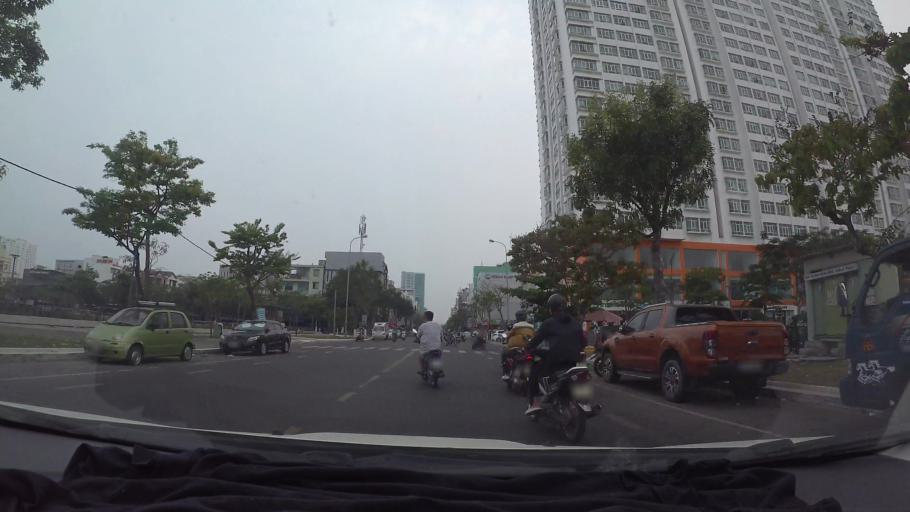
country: VN
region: Da Nang
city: Da Nang
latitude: 16.0632
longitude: 108.2106
